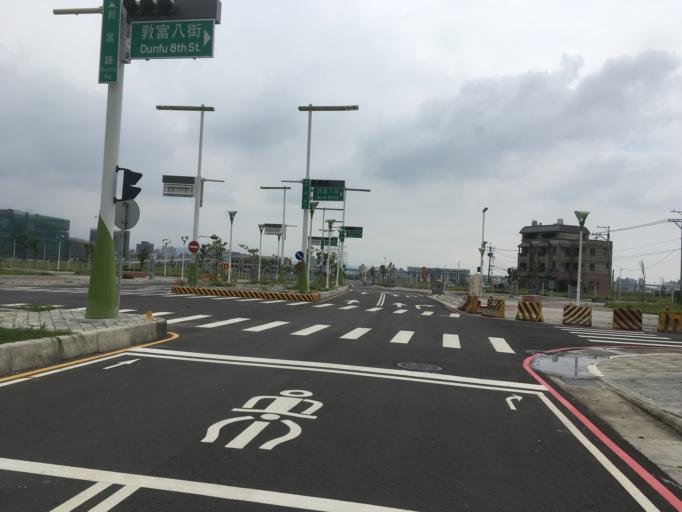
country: TW
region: Taiwan
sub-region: Taichung City
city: Taichung
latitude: 24.1898
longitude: 120.7069
